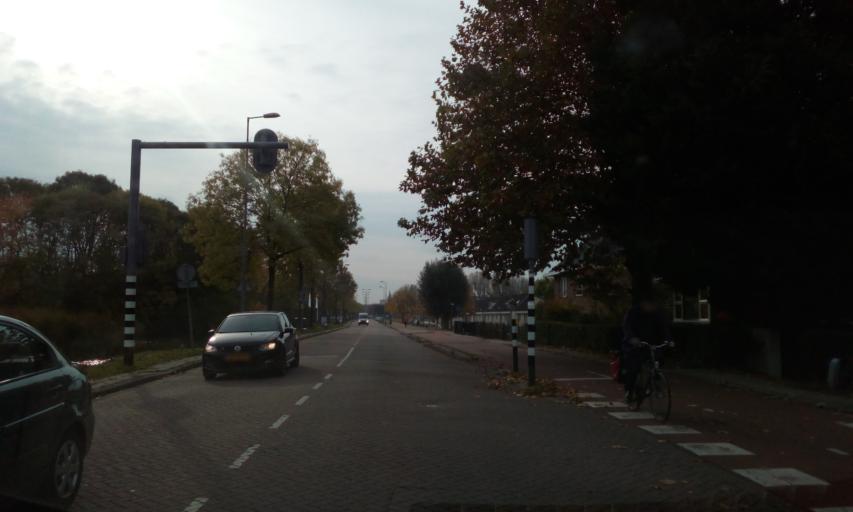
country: NL
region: South Holland
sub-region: Gemeente Rotterdam
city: Rotterdam
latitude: 51.9535
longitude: 4.4770
